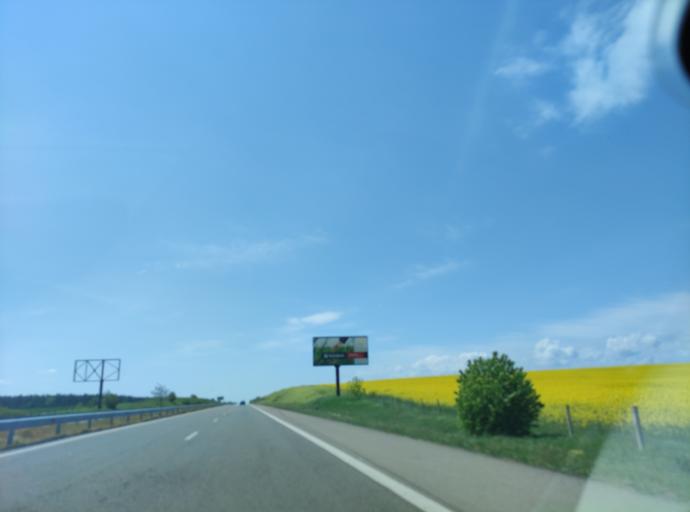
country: BG
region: Burgas
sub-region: Obshtina Karnobat
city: Karnobat
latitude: 42.5899
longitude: 27.0406
